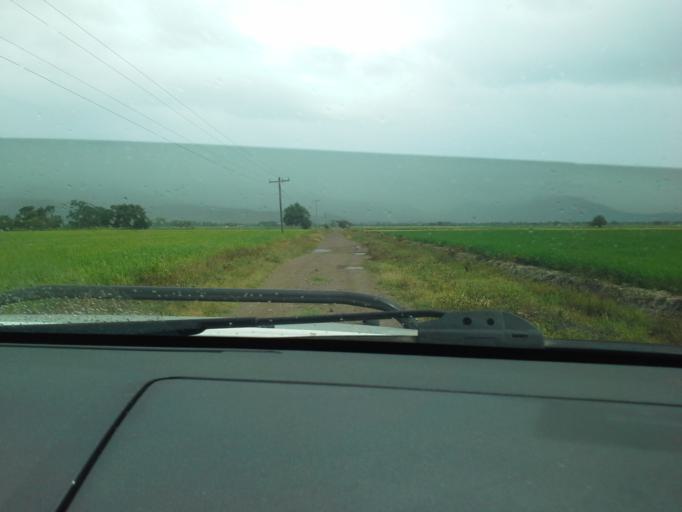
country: NI
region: Matagalpa
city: Ciudad Dario
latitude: 12.8469
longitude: -86.1761
